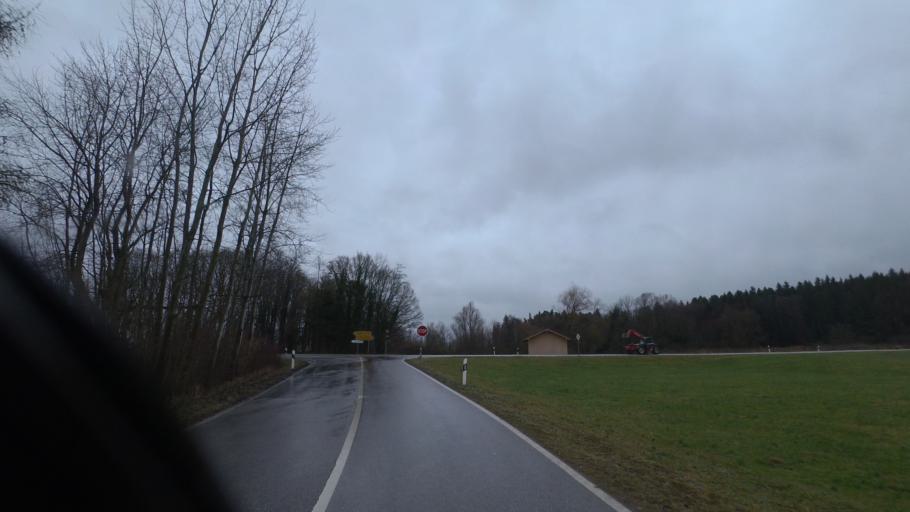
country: DE
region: Bavaria
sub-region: Upper Bavaria
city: Petting
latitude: 47.9106
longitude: 12.8061
